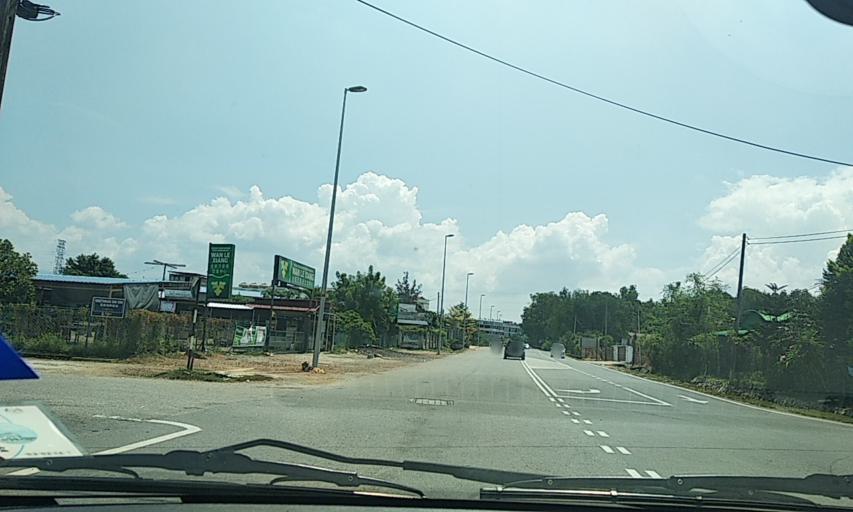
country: MY
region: Kedah
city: Sungai Petani
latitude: 5.6359
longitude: 100.4820
